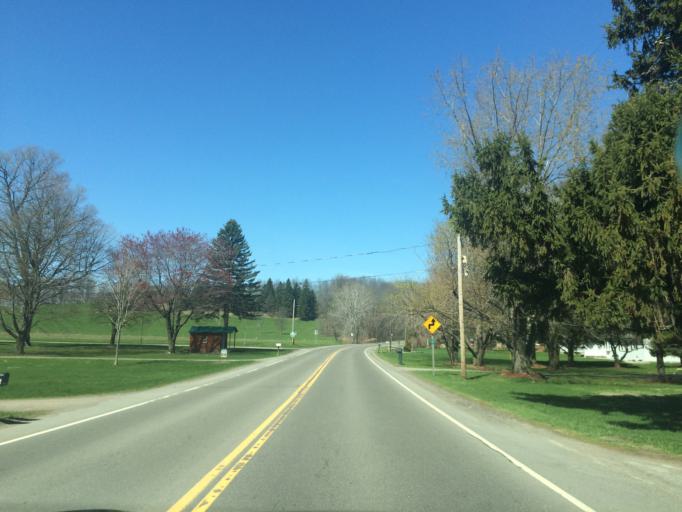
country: US
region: New York
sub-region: Wayne County
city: Macedon
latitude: 43.0941
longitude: -77.3553
